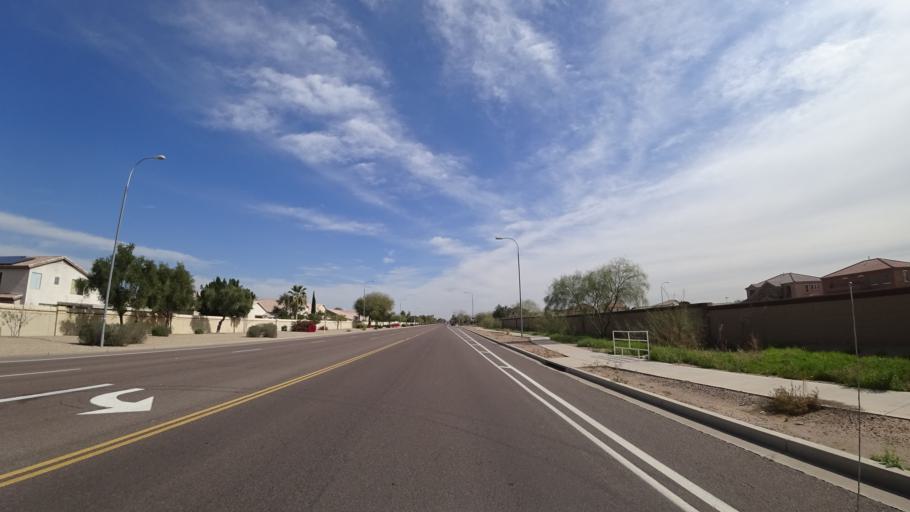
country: US
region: Arizona
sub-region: Maricopa County
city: Tolleson
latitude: 33.4785
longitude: -112.3047
